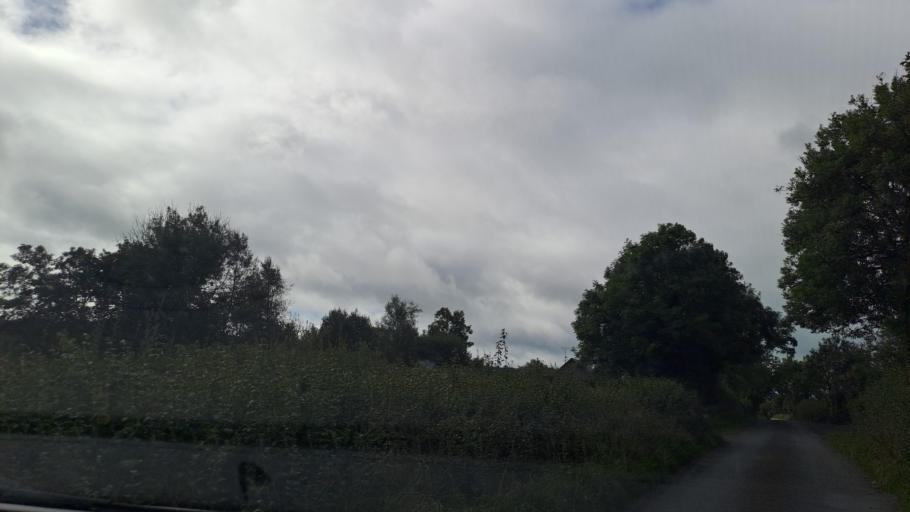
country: IE
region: Ulster
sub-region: An Cabhan
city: Bailieborough
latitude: 53.9713
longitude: -6.8904
